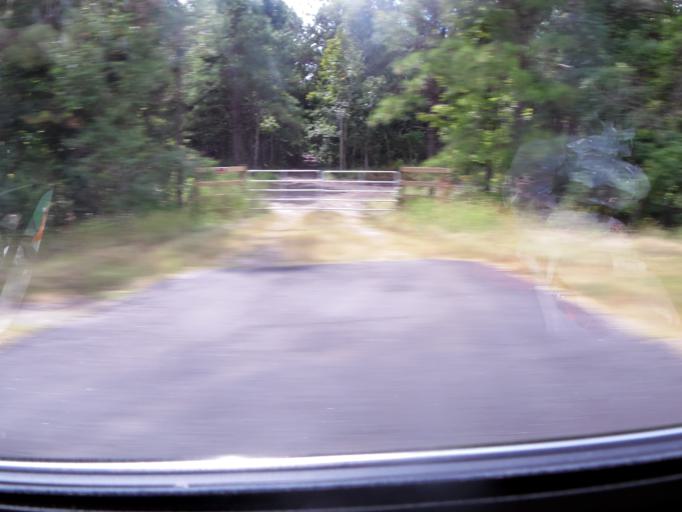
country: US
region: Georgia
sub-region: Glynn County
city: Dock Junction
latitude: 31.1612
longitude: -81.5949
